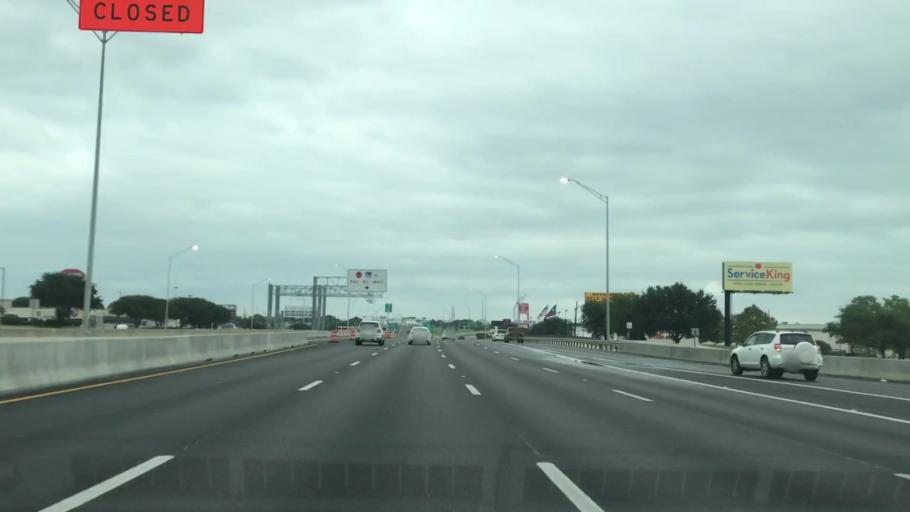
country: US
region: Texas
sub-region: Dallas County
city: Irving
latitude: 32.8370
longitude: -97.0037
